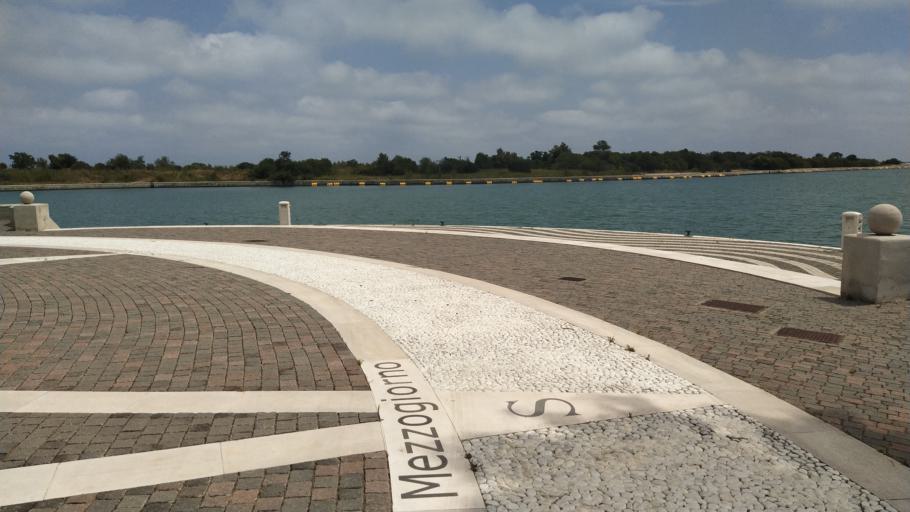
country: IT
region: Apulia
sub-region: Provincia di Taranto
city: Marina di Ginosa
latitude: 40.3387
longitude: 16.8126
